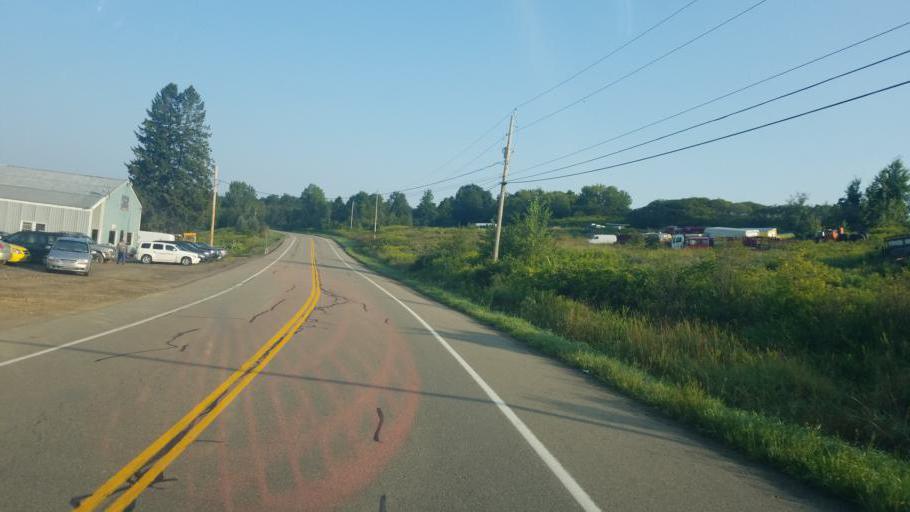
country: US
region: Pennsylvania
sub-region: Tioga County
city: Westfield
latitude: 42.0185
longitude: -77.5221
